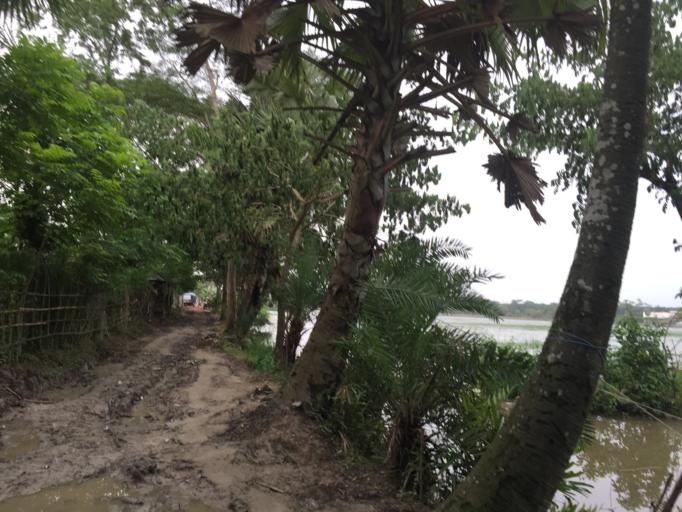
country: BD
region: Barisal
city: Mathba
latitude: 22.1921
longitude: 89.9312
